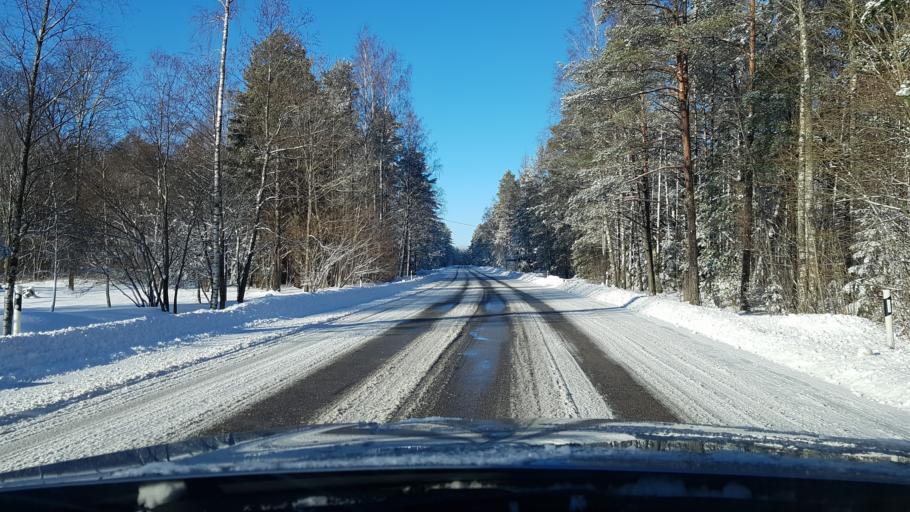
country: EE
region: Hiiumaa
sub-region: Kaerdla linn
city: Kardla
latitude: 58.9225
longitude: 22.7935
